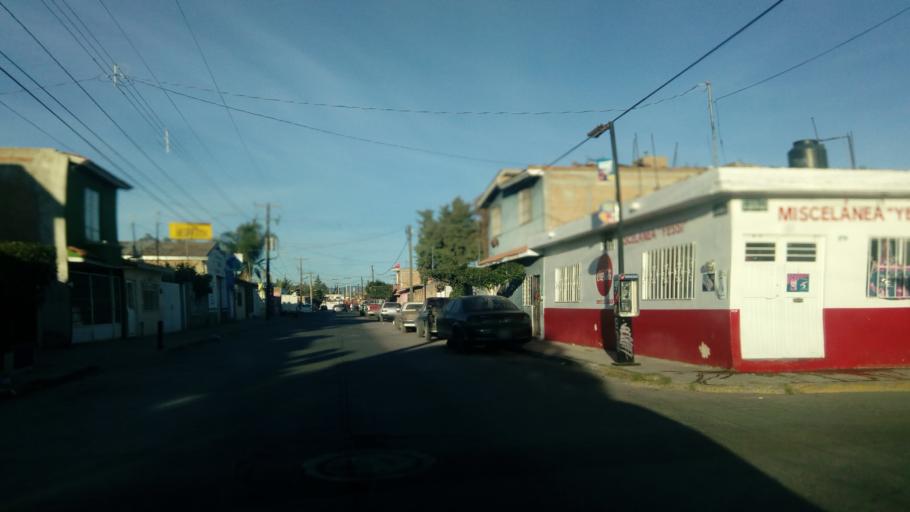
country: MX
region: Durango
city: Victoria de Durango
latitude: 24.0029
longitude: -104.6583
